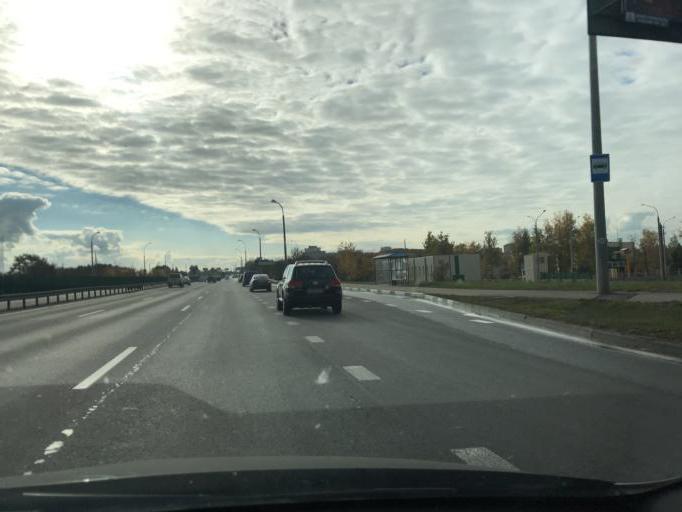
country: BY
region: Minsk
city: Vyaliki Trastsyanets
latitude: 53.8488
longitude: 27.6709
